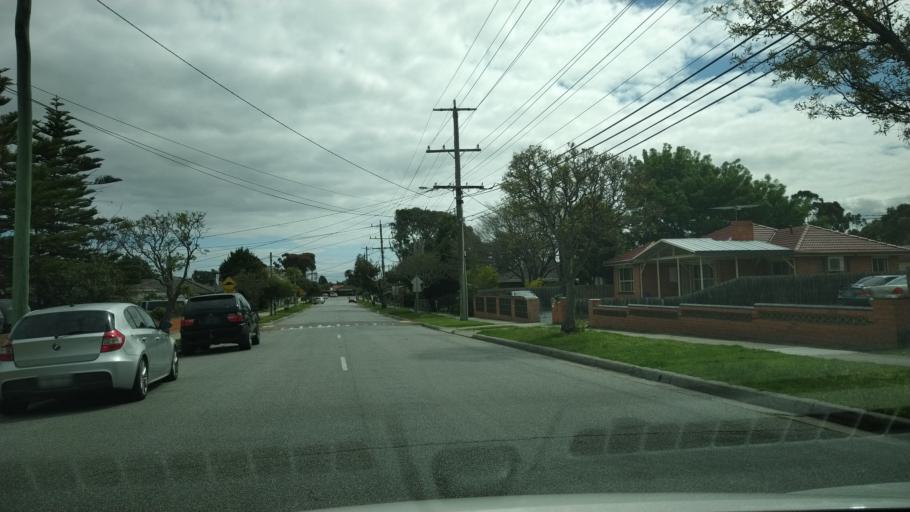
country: AU
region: Victoria
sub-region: Greater Dandenong
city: Noble Park
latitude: -37.9792
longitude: 145.1690
